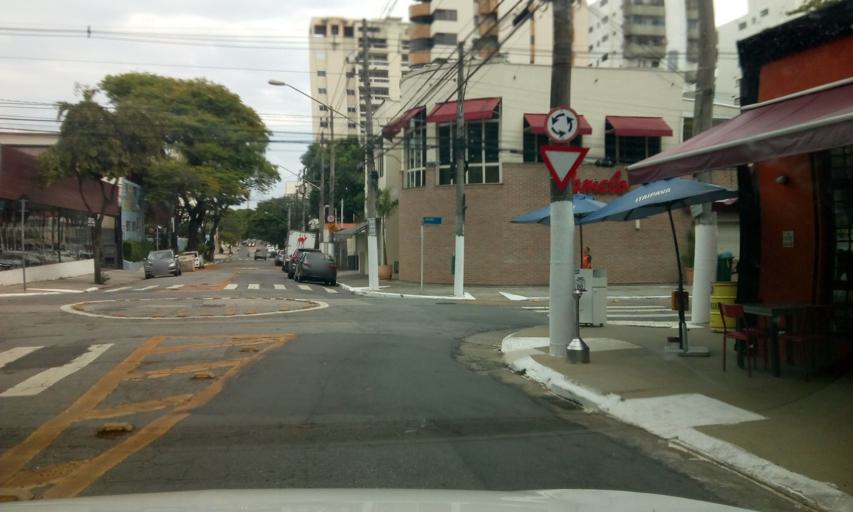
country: BR
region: Sao Paulo
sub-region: Sao Paulo
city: Sao Paulo
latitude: -23.6119
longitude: -46.6595
